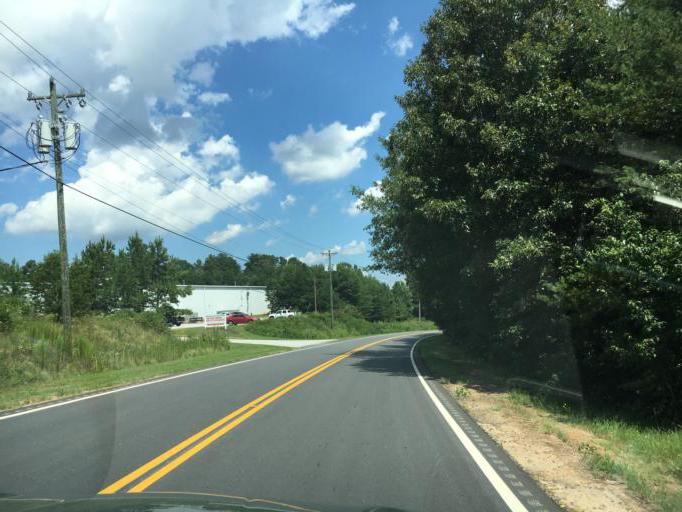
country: US
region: South Carolina
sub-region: Spartanburg County
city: Duncan
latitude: 34.9047
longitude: -82.1474
